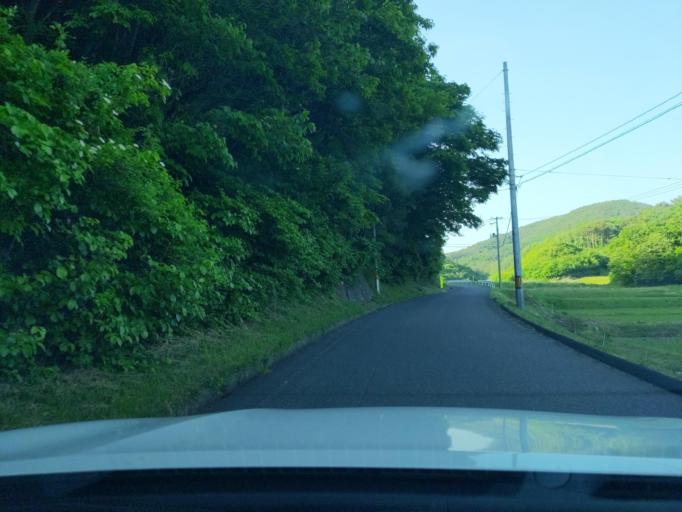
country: JP
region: Fukushima
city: Motomiya
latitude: 37.5158
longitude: 140.3294
